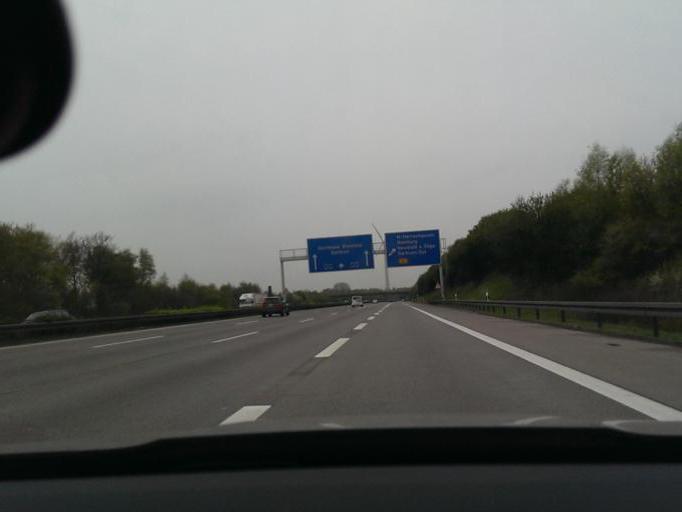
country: DE
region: Lower Saxony
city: Garbsen-Mitte
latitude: 52.4229
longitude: 9.6412
